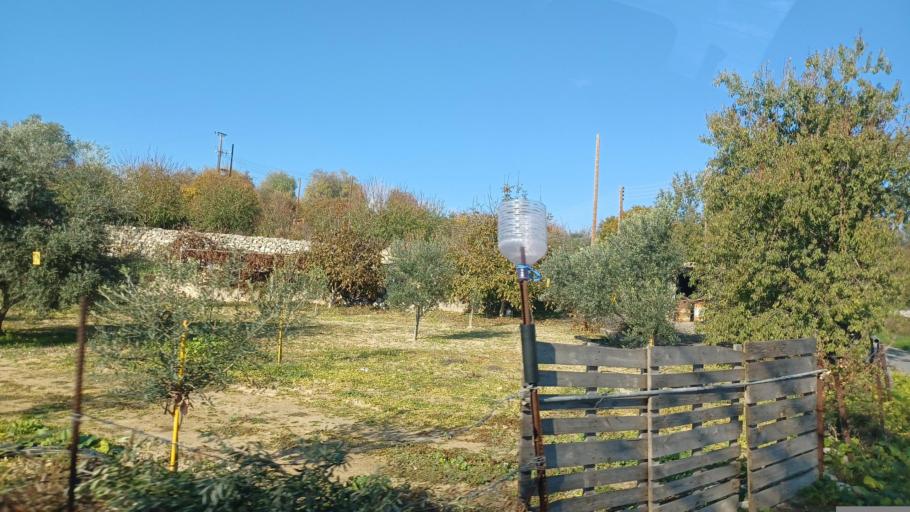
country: CY
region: Pafos
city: Mesogi
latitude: 34.8465
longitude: 32.5260
